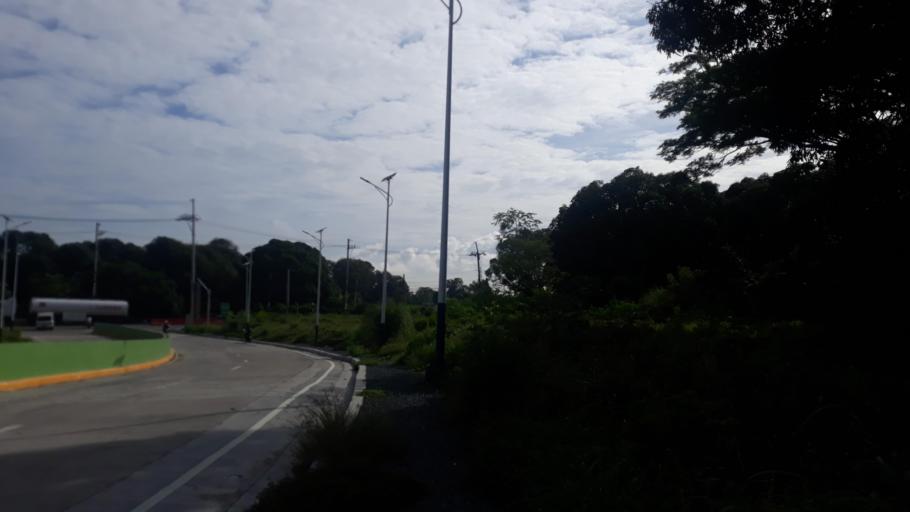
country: PH
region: Calabarzon
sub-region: Province of Cavite
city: Bulihan
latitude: 14.2924
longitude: 120.9704
